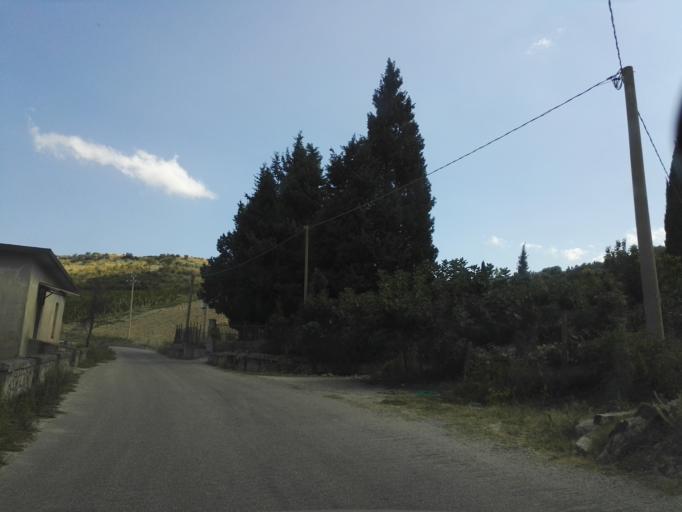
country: IT
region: Calabria
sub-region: Provincia di Reggio Calabria
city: Stilo
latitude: 38.4615
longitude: 16.4947
